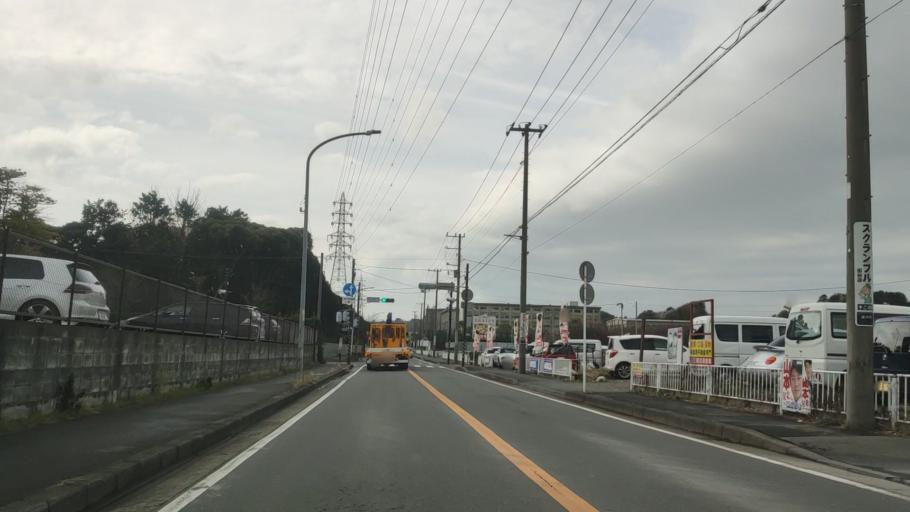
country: JP
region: Kanagawa
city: Fujisawa
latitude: 35.3772
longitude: 139.5254
